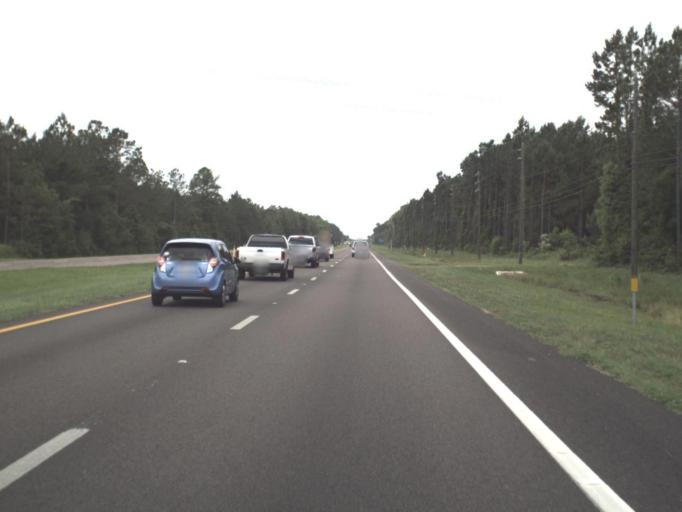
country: US
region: Florida
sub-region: Nassau County
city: Yulee
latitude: 30.6263
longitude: -81.6258
